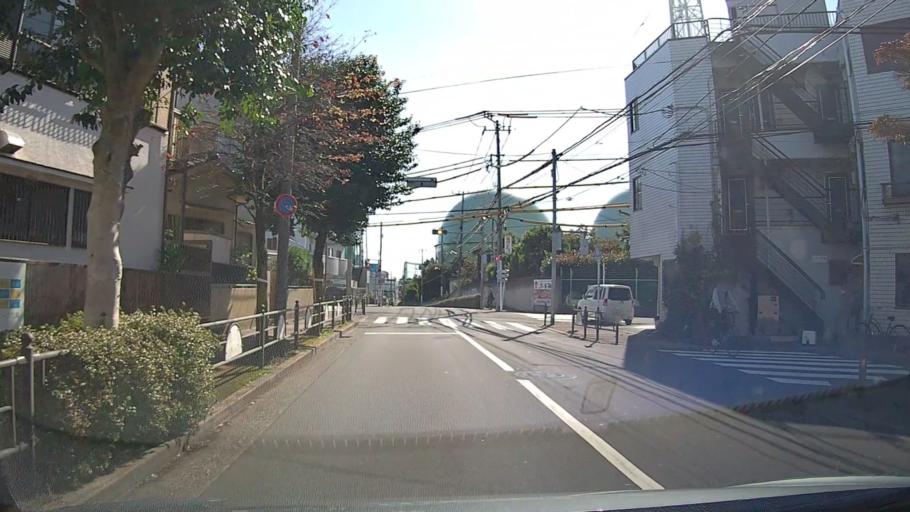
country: JP
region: Saitama
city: Wako
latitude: 35.7489
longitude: 139.6257
